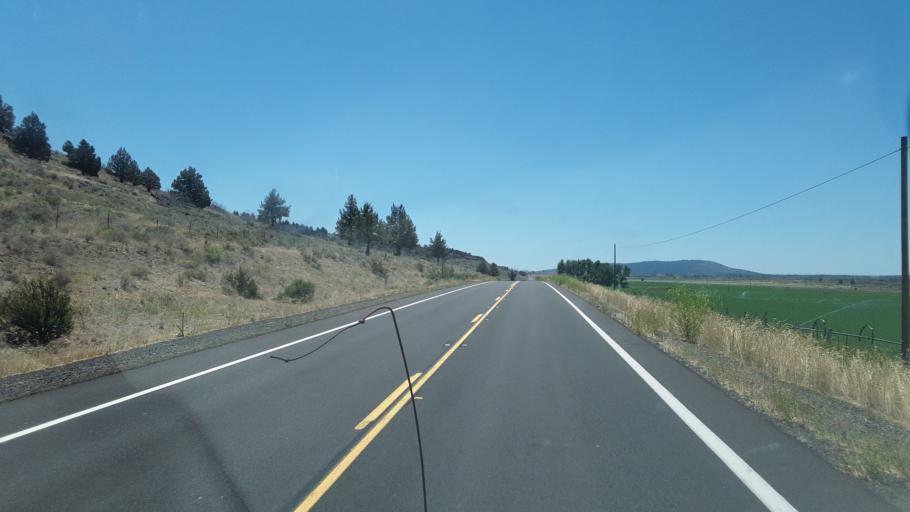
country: US
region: California
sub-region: Siskiyou County
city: Tulelake
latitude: 41.7431
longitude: -121.3006
